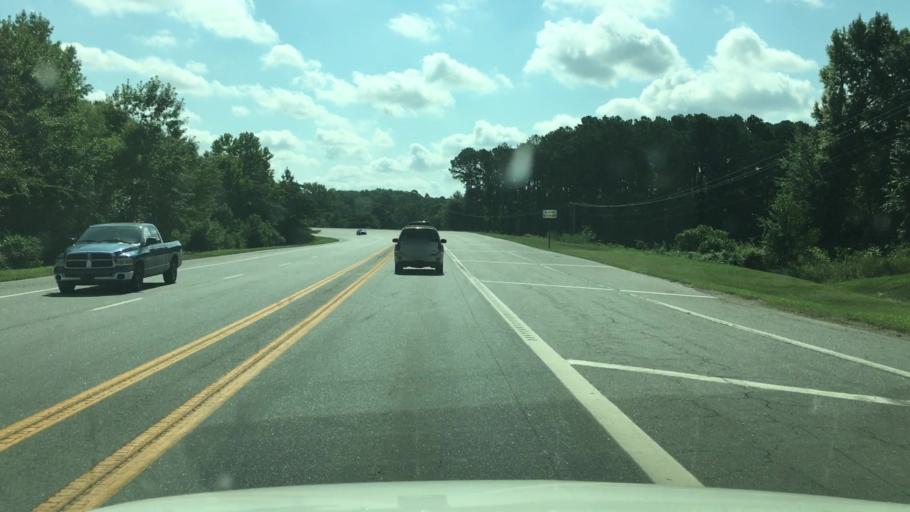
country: US
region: Arkansas
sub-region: Garland County
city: Piney
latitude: 34.5073
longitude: -93.1874
